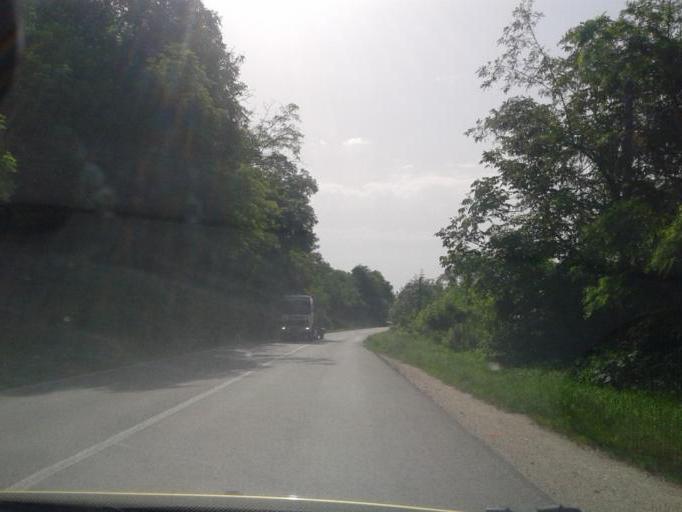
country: RO
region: Valcea
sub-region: Comuna Bunesti
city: Bunesti
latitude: 45.1114
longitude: 24.1791
